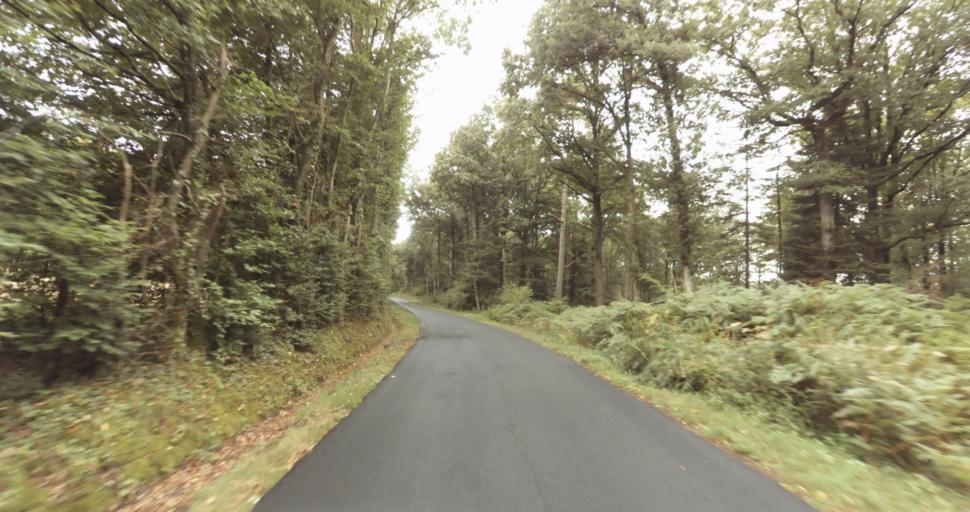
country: FR
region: Lower Normandy
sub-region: Departement de l'Orne
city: Sainte-Gauburge-Sainte-Colombe
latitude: 48.7538
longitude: 0.4867
